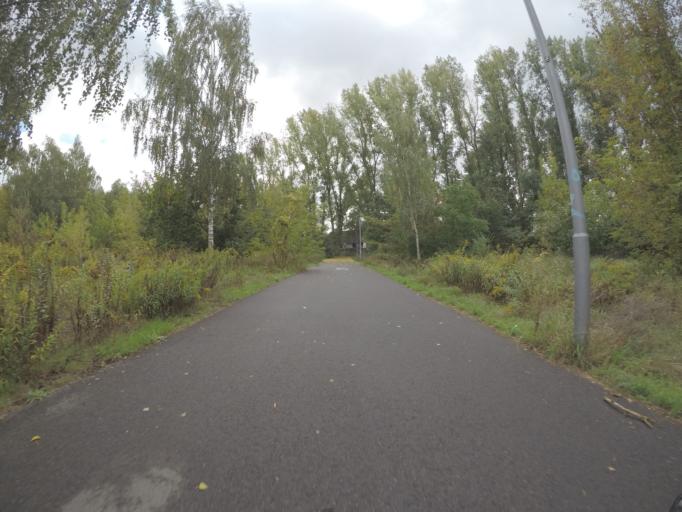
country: DE
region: Berlin
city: Stadtrandsiedlung Malchow
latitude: 52.5648
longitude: 13.4856
